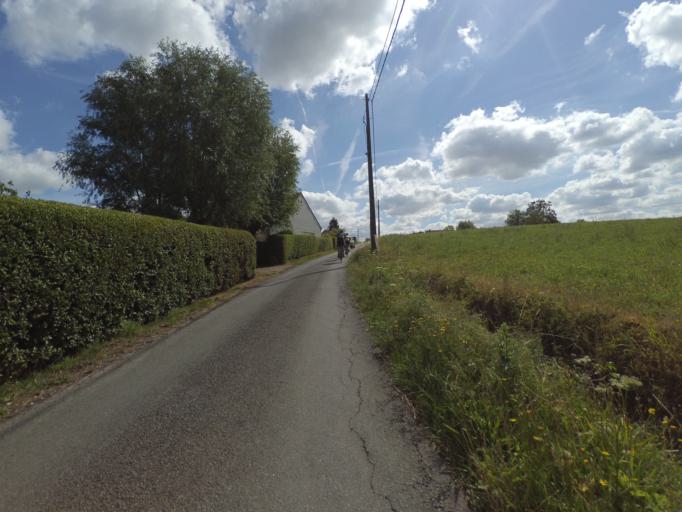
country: BE
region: Wallonia
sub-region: Province du Hainaut
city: Frasnes-lez-Anvaing
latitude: 50.7228
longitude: 3.6383
